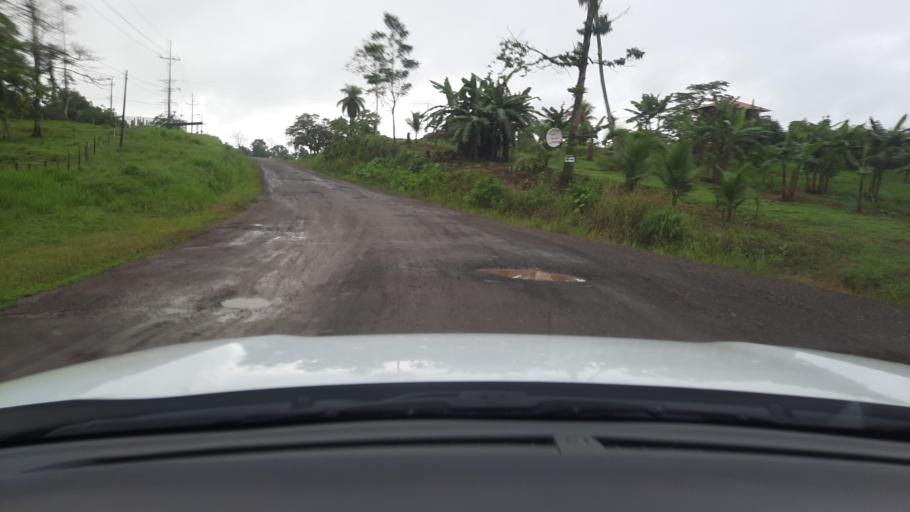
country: CR
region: Alajuela
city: San Jose
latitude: 11.0031
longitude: -85.3160
